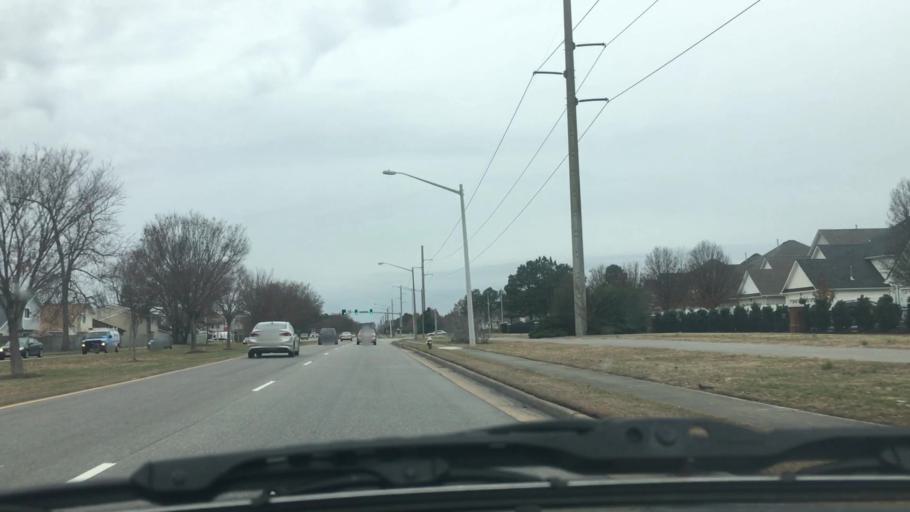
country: US
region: Virginia
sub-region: City of Virginia Beach
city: Virginia Beach
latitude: 36.8051
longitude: -76.1155
